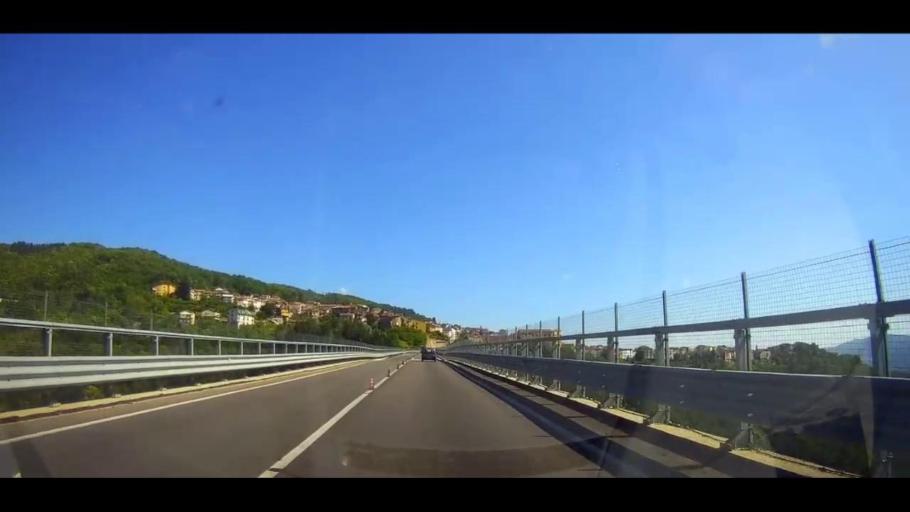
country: IT
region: Calabria
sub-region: Provincia di Cosenza
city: Celico
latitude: 39.3155
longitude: 16.3338
